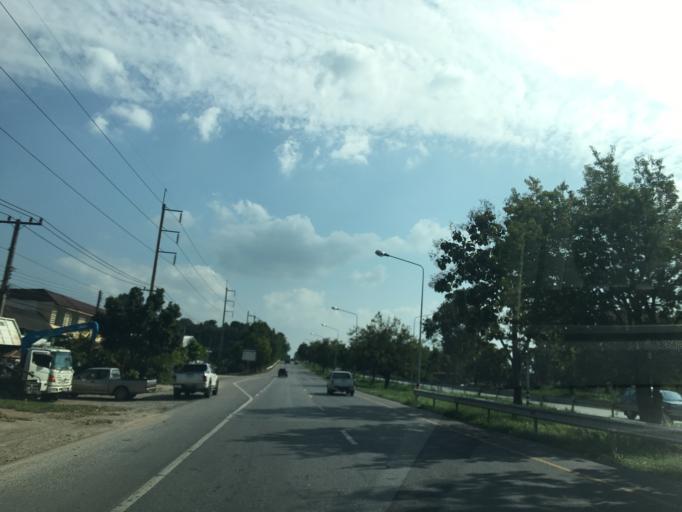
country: TH
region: Chiang Rai
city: Mae Lao
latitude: 19.7006
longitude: 99.7199
